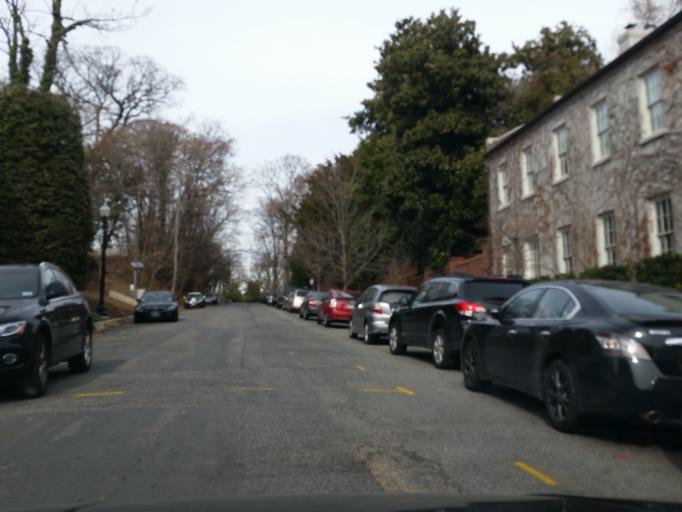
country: US
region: Washington, D.C.
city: Washington, D.C.
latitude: 38.9108
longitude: -77.0571
